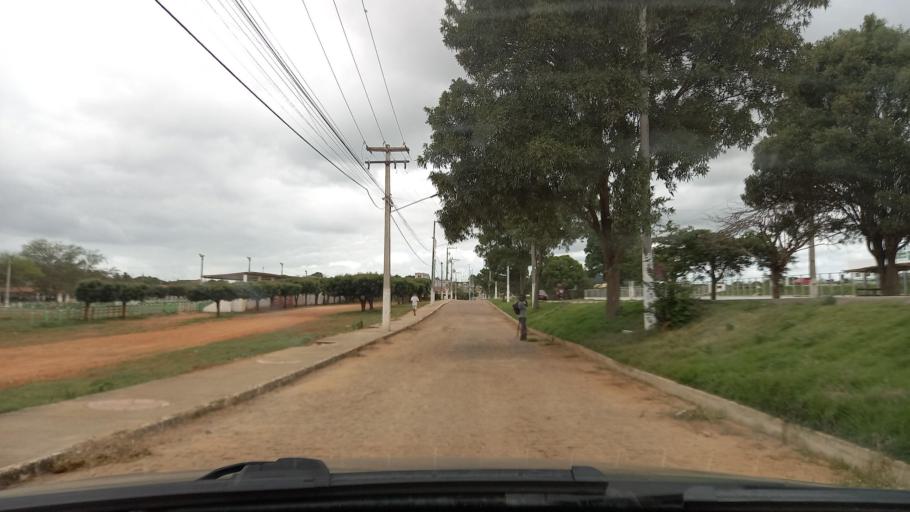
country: BR
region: Sergipe
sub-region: Caninde De Sao Francisco
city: Caninde de Sao Francisco
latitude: -9.6682
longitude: -37.7935
